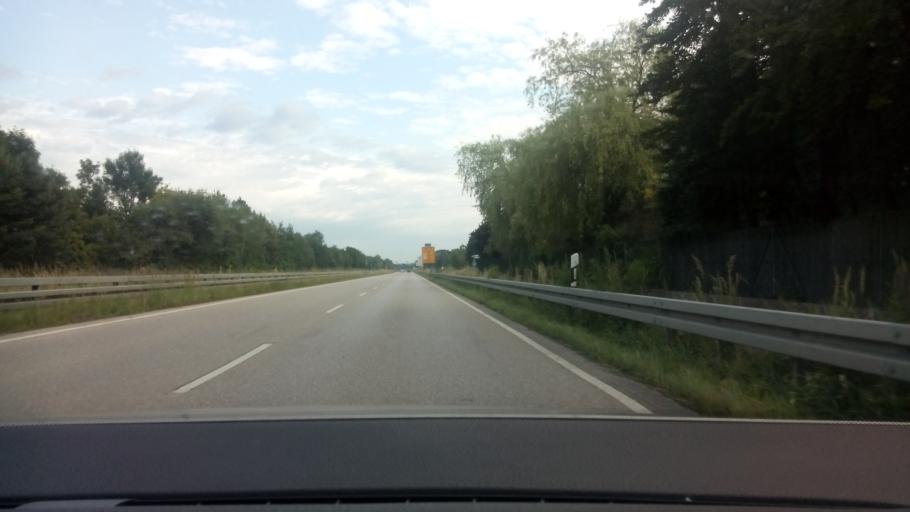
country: DE
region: Bavaria
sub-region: Upper Bavaria
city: Unterschleissheim
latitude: 48.2600
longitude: 11.5975
